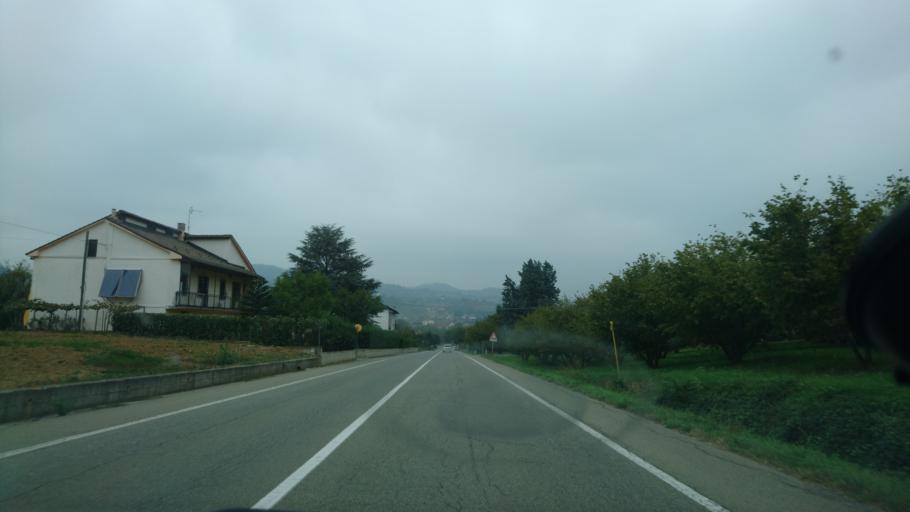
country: IT
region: Piedmont
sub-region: Provincia di Alessandria
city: Bistagno
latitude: 44.6539
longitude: 8.3636
